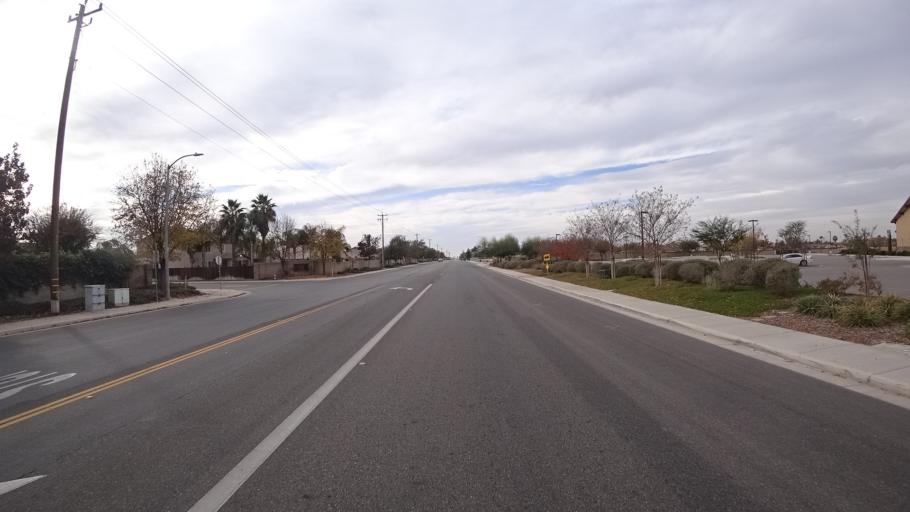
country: US
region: California
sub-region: Kern County
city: Rosedale
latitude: 35.4125
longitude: -119.1384
